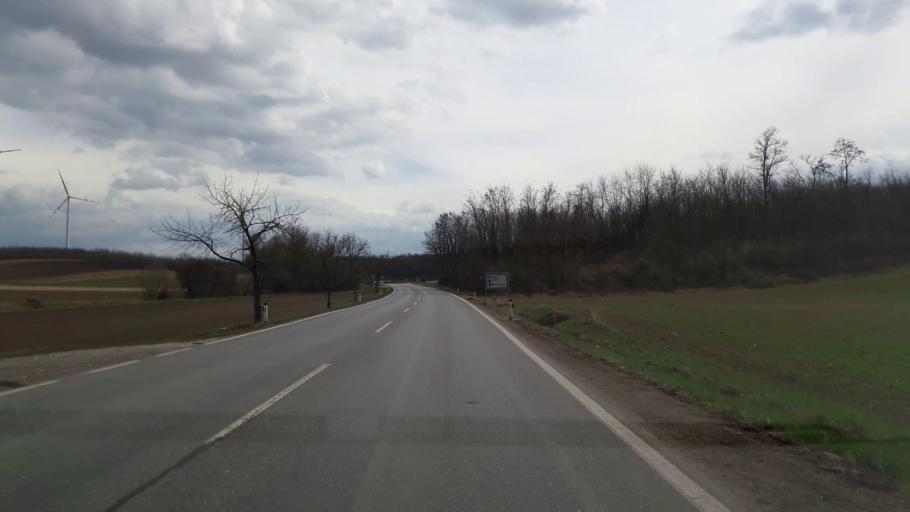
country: AT
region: Lower Austria
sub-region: Politischer Bezirk Mistelbach
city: Mistelbach
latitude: 48.5445
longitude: 16.5894
